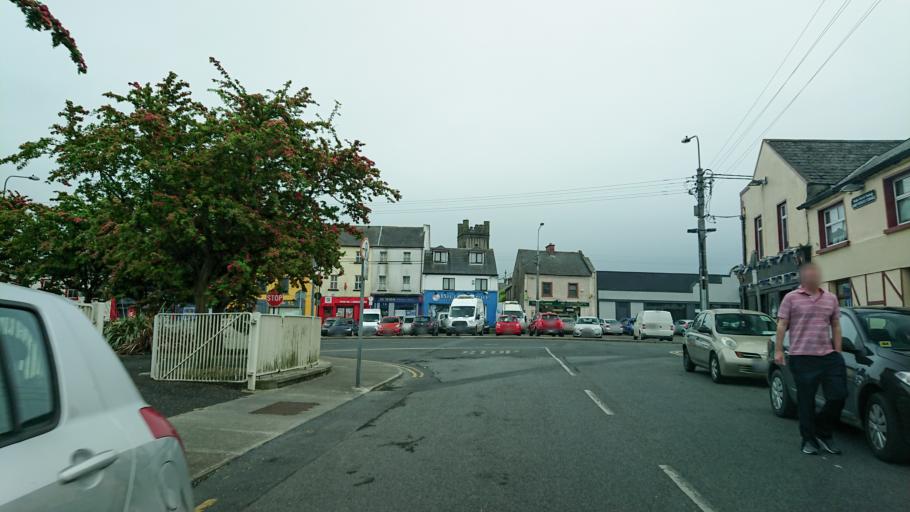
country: IE
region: Munster
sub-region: Waterford
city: Waterford
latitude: 52.2604
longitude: -7.1161
